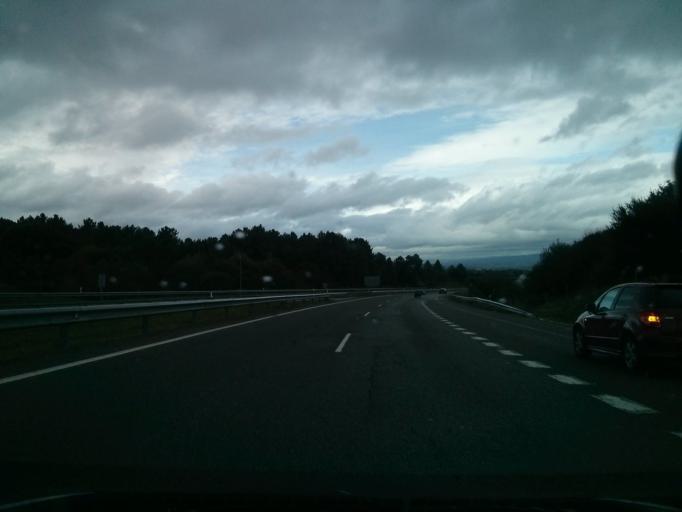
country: ES
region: Galicia
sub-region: Provincia de Ourense
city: Taboadela
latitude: 42.2527
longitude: -7.8675
